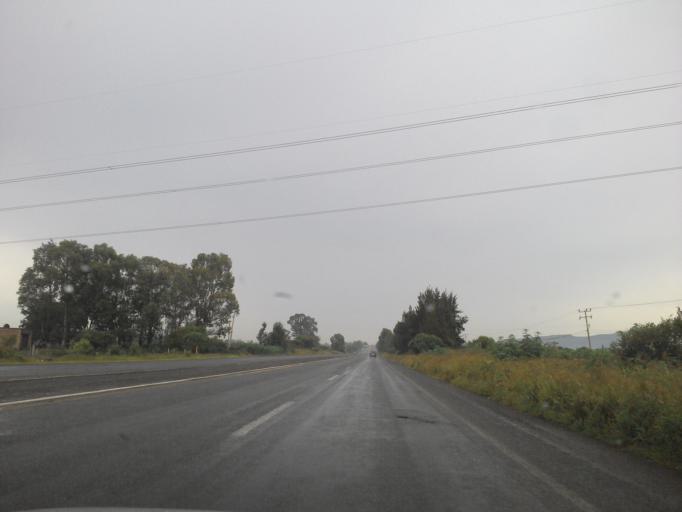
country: MX
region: Jalisco
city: Tepatitlan de Morelos
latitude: 20.8799
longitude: -102.6911
